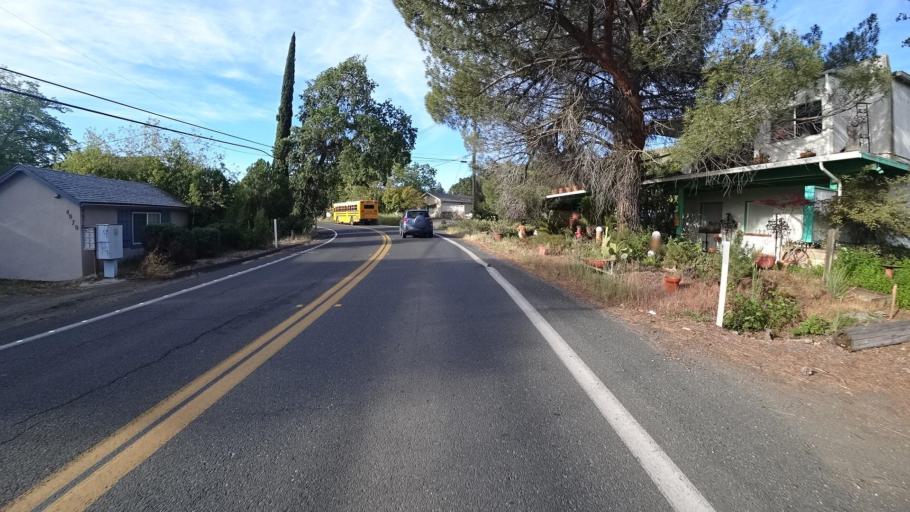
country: US
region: California
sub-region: Lake County
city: North Lakeport
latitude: 39.0897
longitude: -122.9036
